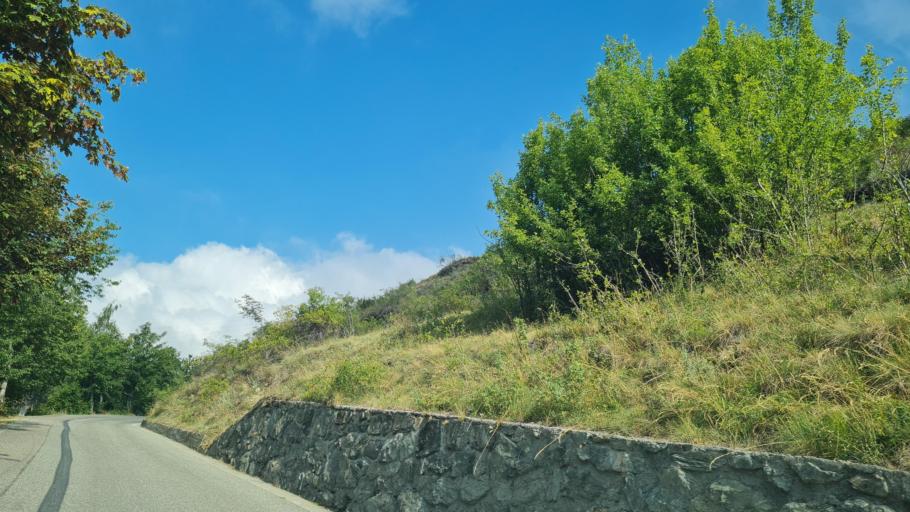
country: IT
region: Aosta Valley
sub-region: Valle d'Aosta
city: La Magdeleine
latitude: 45.8133
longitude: 7.6076
